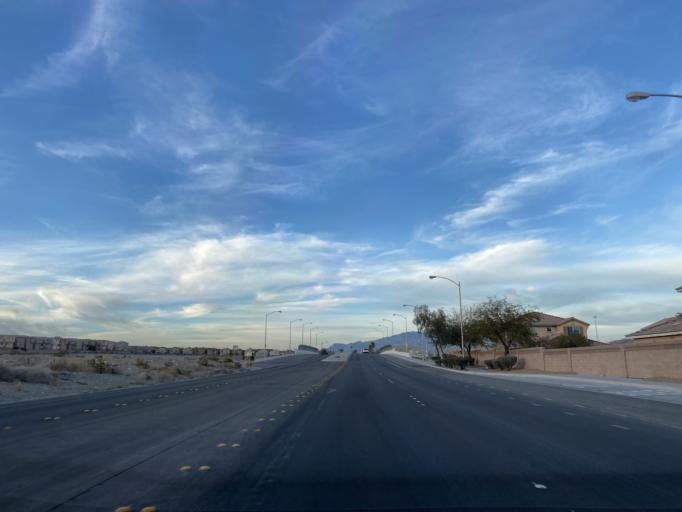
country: US
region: Nevada
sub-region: Clark County
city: Summerlin South
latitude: 36.2783
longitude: -115.2969
